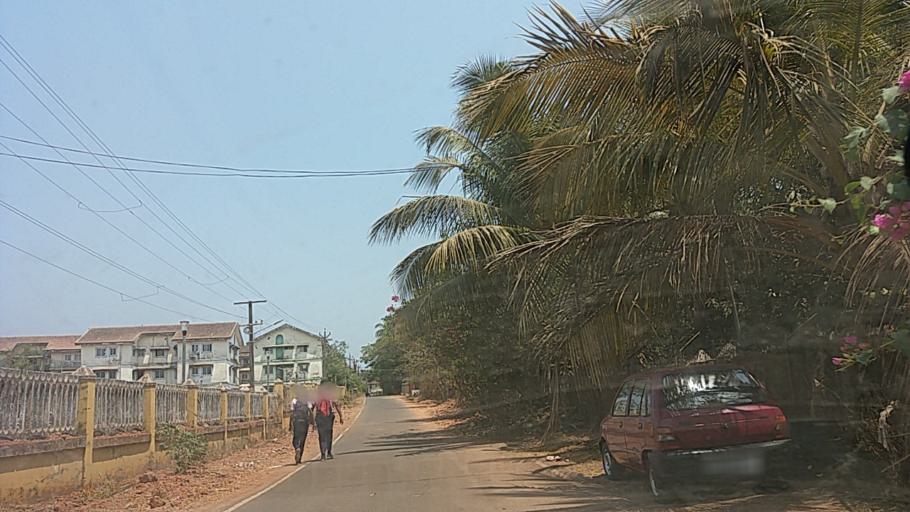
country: IN
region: Goa
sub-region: North Goa
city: Serula
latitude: 15.5238
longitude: 73.8314
